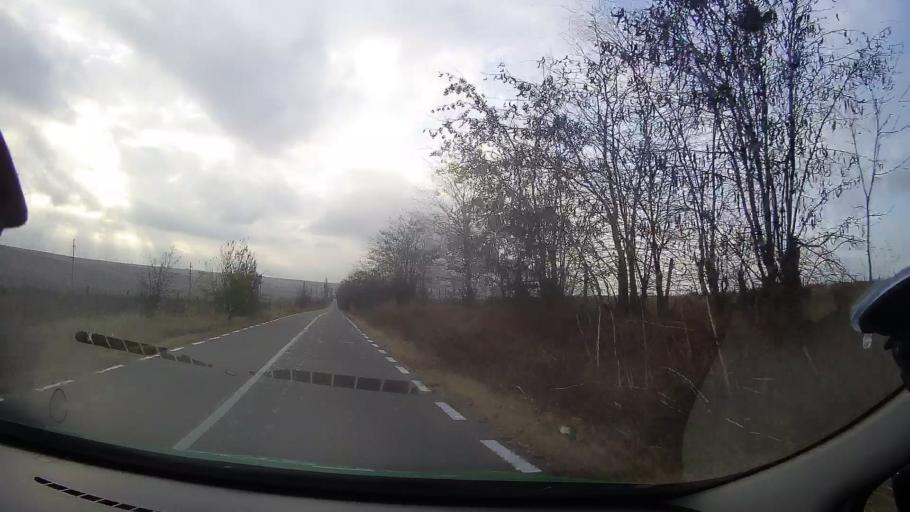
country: RO
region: Constanta
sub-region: Municipiul Medgidia
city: Medgidia
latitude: 44.2378
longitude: 28.2477
